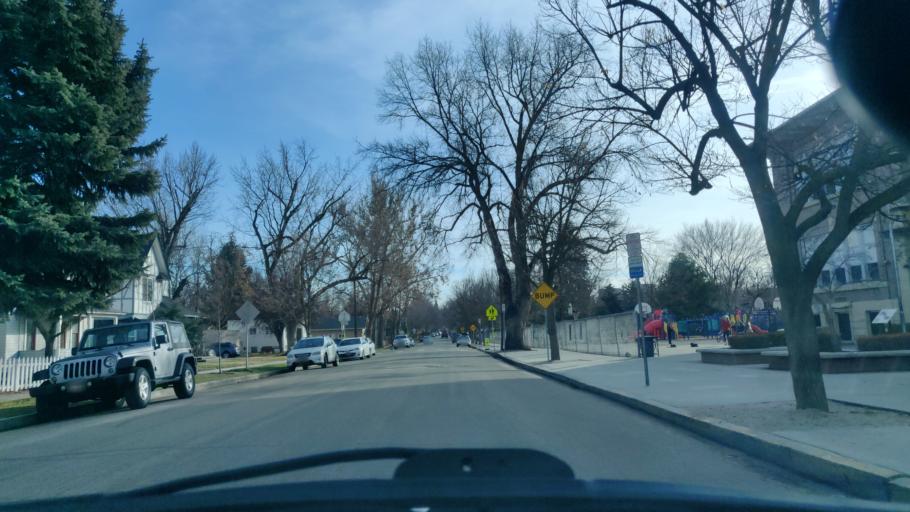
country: US
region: Idaho
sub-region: Ada County
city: Boise
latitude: 43.6281
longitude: -116.1987
